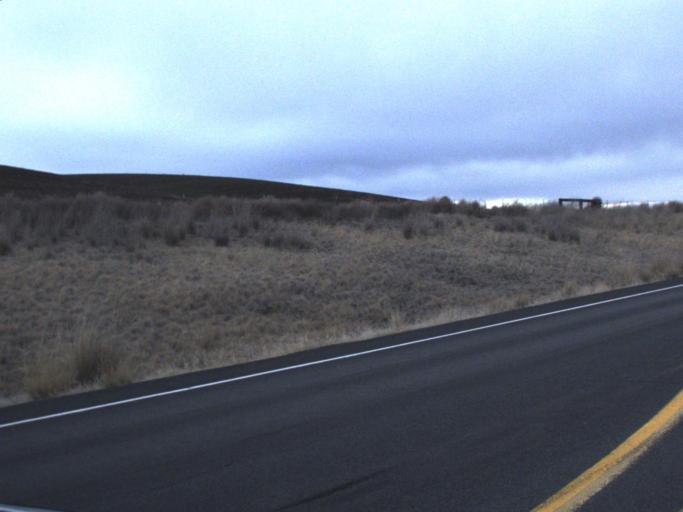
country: US
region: Washington
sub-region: Whitman County
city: Colfax
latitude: 46.8102
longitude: -117.6425
